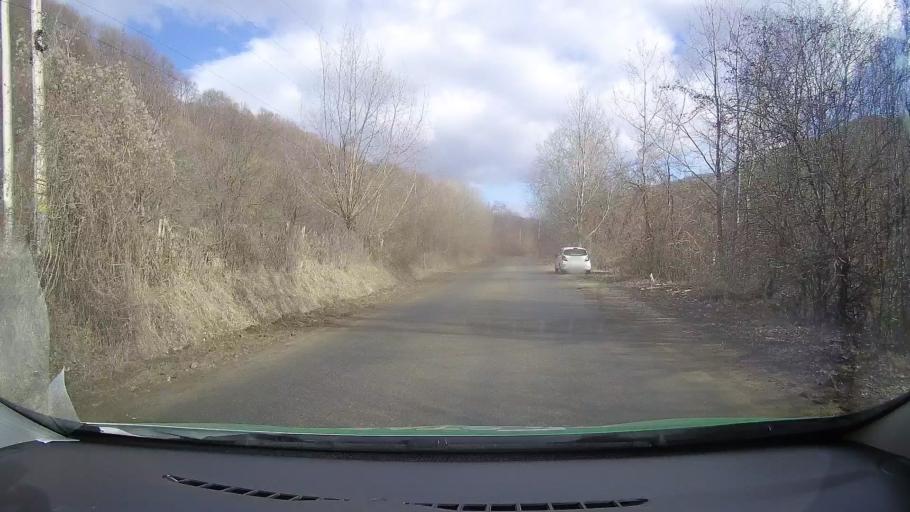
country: RO
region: Dambovita
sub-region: Comuna Motaeni
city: Motaeni
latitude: 45.1037
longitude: 25.4405
